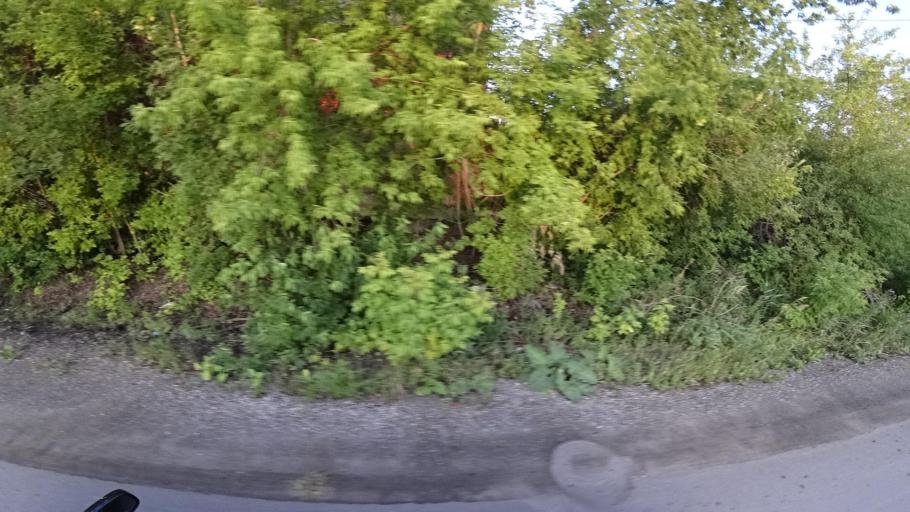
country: RU
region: Sverdlovsk
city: Kamyshlov
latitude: 56.8496
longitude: 62.7350
